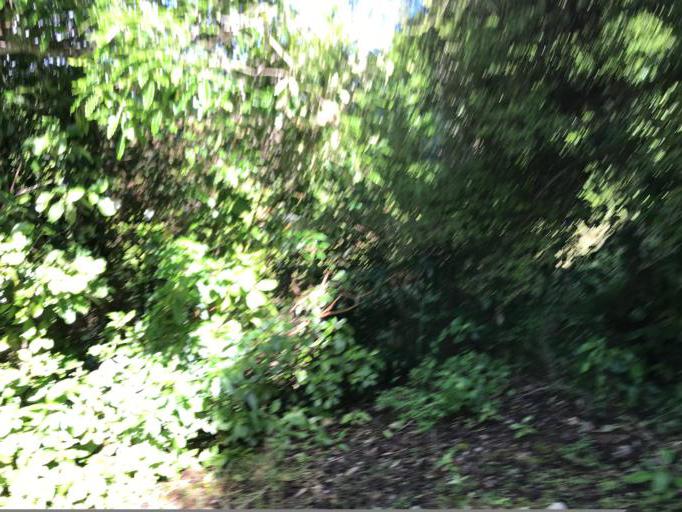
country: NZ
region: Wellington
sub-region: Kapiti Coast District
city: Otaki
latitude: -40.8755
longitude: 175.2348
